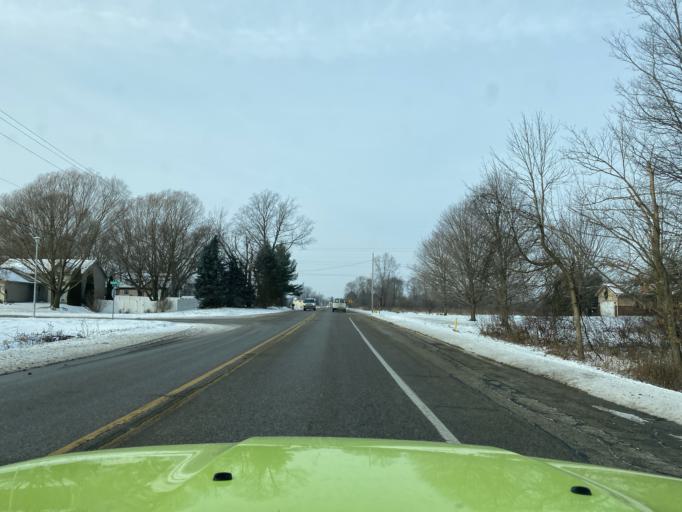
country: US
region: Michigan
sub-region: Ottawa County
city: Hudsonville
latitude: 42.8853
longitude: -85.8961
